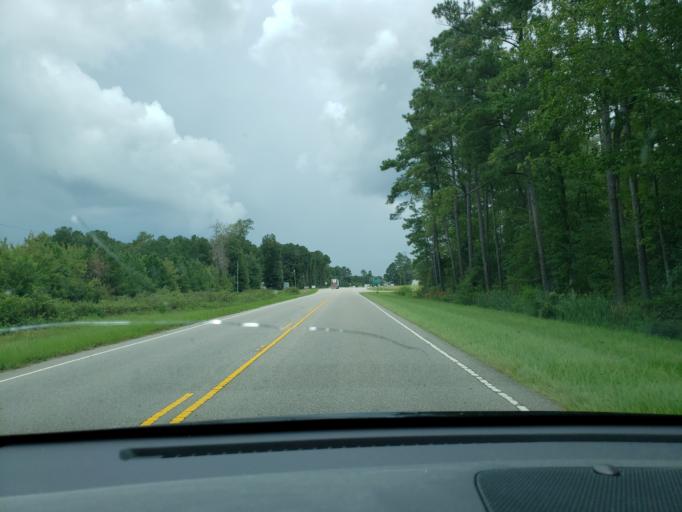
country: US
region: North Carolina
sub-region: Bladen County
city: Bladenboro
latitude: 34.4825
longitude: -78.6651
